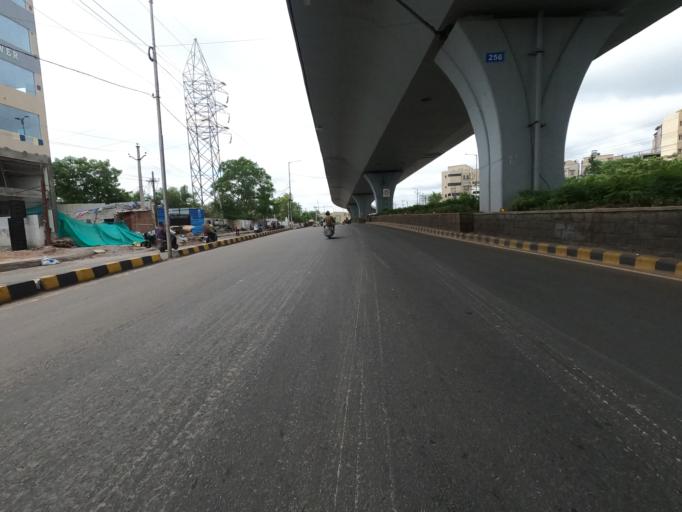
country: IN
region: Telangana
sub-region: Hyderabad
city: Hyderabad
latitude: 17.3382
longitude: 78.4257
